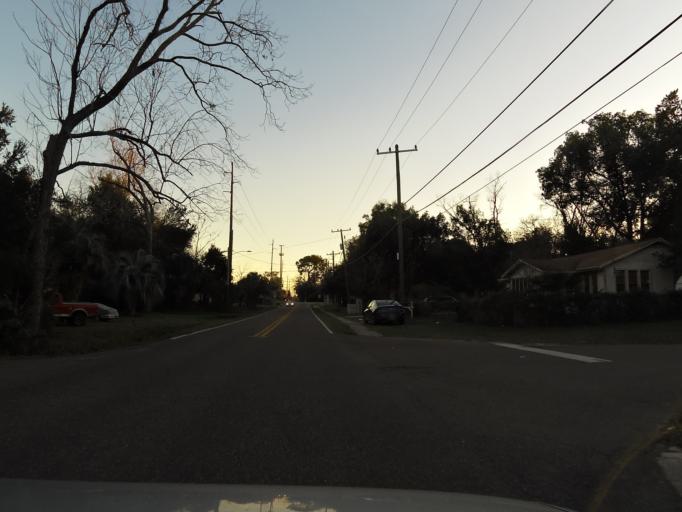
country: US
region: Florida
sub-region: Duval County
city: Jacksonville
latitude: 30.2903
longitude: -81.7222
